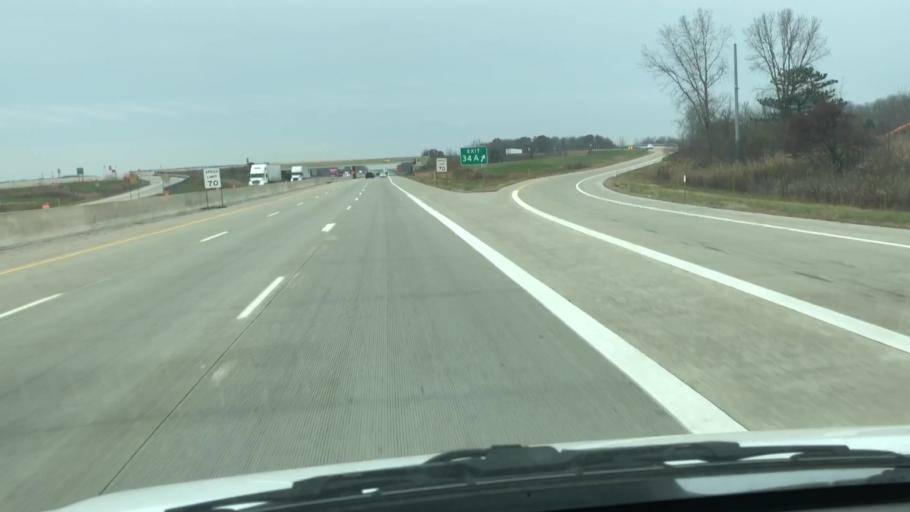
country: US
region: Michigan
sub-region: Wayne County
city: Woodhaven
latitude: 42.1688
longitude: -83.2433
